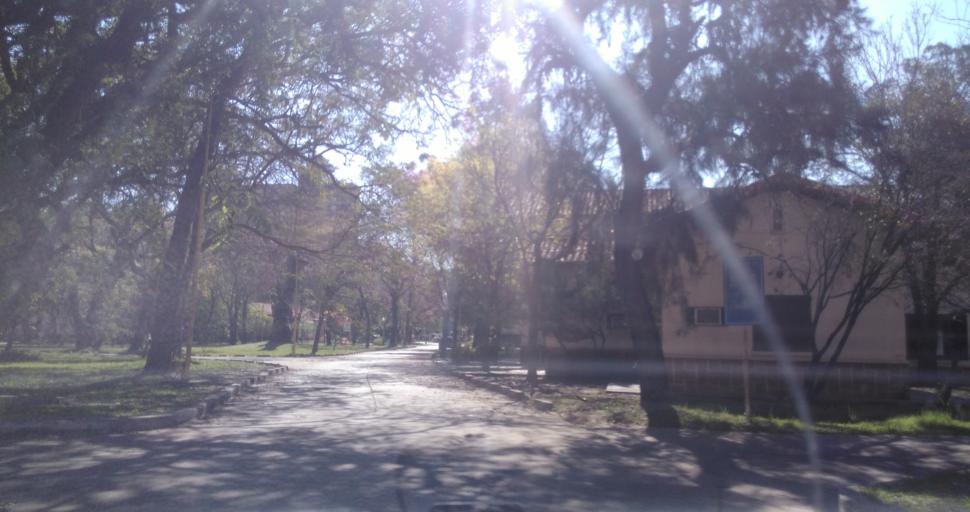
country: AR
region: Chaco
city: Resistencia
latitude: -27.4640
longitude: -58.9830
